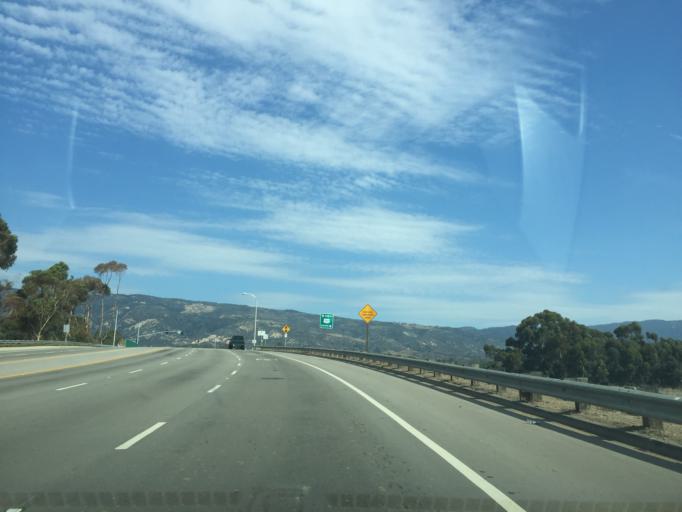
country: US
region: California
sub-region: Santa Barbara County
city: Isla Vista
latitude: 34.4352
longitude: -119.8529
